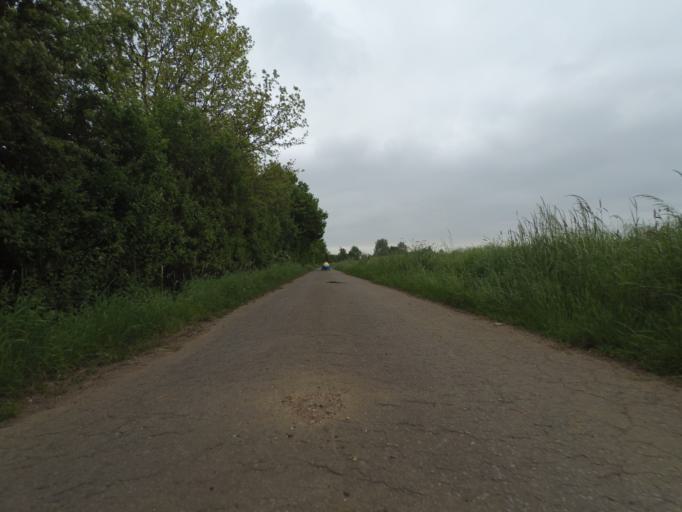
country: DE
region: Lower Saxony
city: Haenigsen
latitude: 52.4827
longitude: 10.0577
